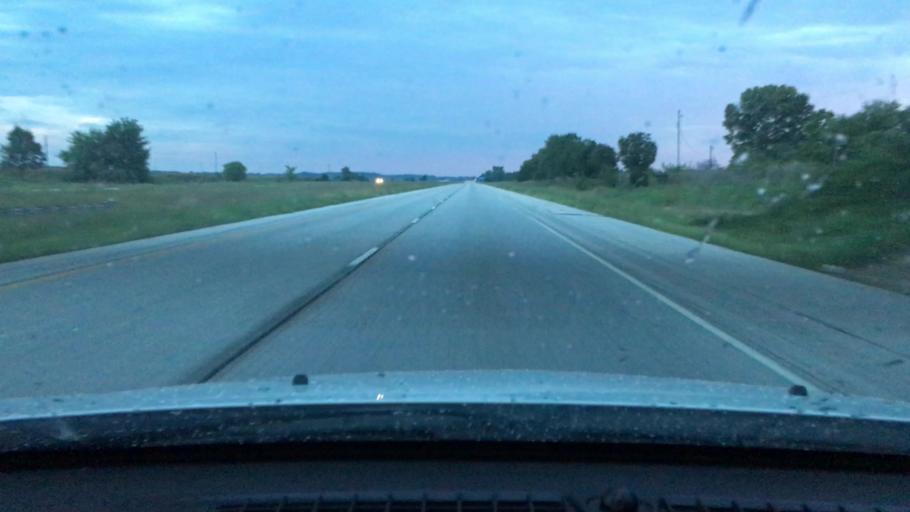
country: US
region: Illinois
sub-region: Morgan County
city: South Jacksonville
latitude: 39.7018
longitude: -90.1895
